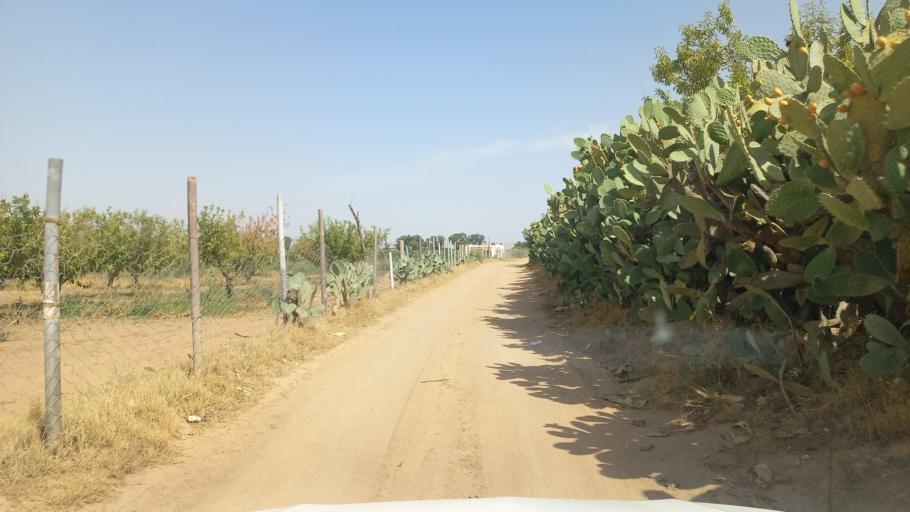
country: TN
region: Al Qasrayn
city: Kasserine
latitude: 35.2555
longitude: 9.0441
